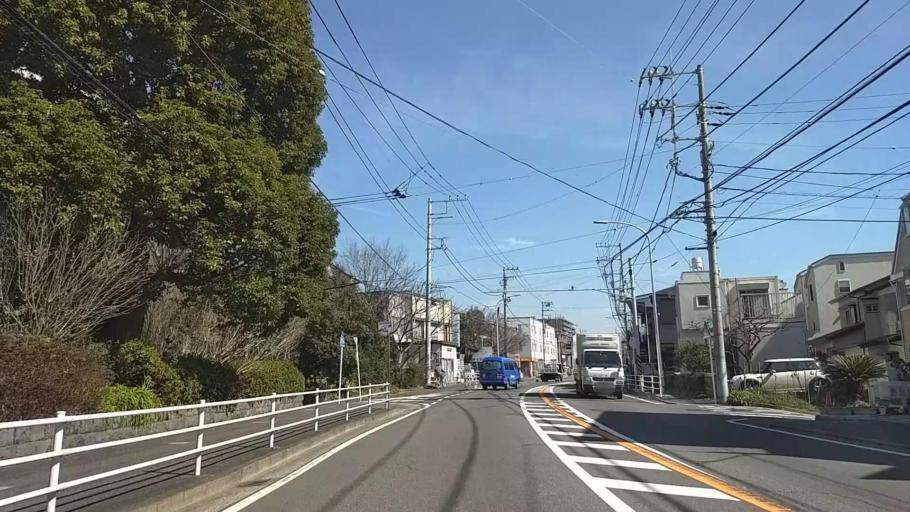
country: JP
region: Kanagawa
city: Kamakura
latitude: 35.3582
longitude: 139.5340
